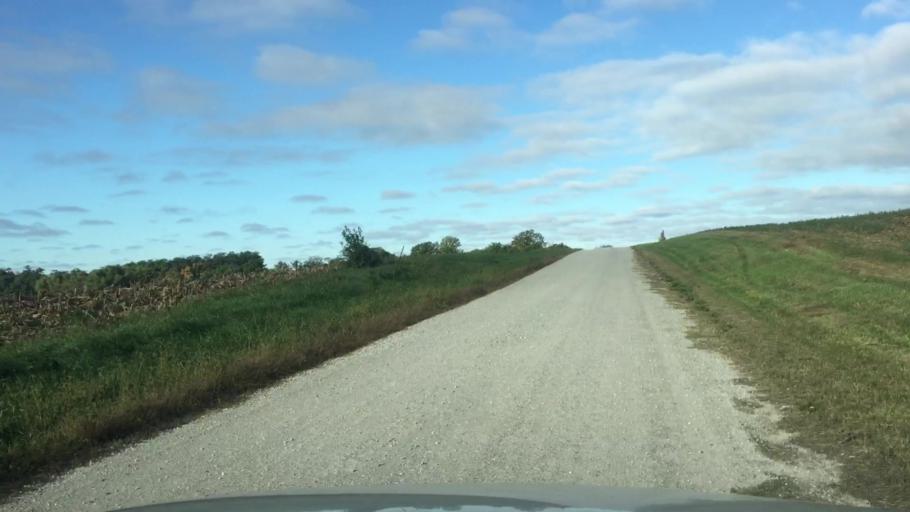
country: US
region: Missouri
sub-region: Howard County
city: New Franklin
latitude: 39.0791
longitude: -92.7475
